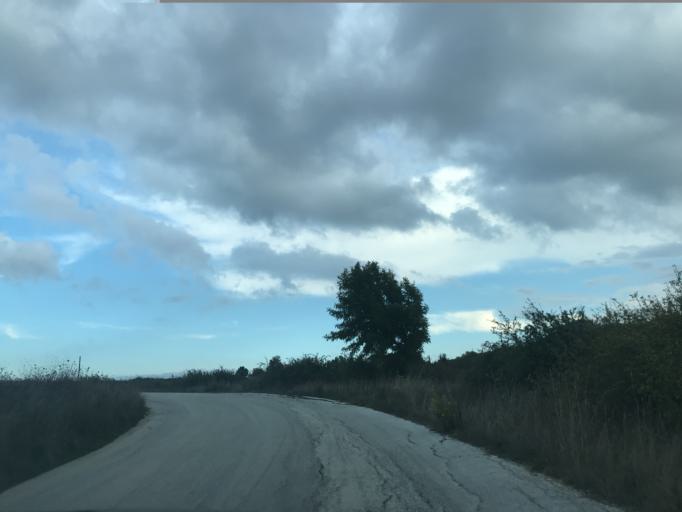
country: IT
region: Molise
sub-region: Provincia di Campobasso
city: Duronia
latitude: 41.6727
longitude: 14.4582
